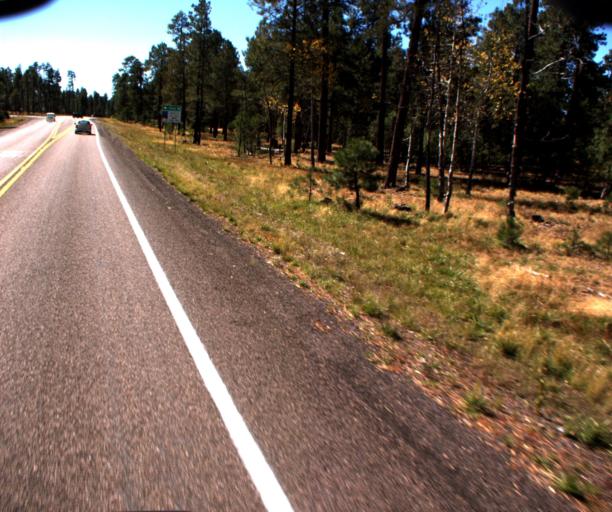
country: US
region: Arizona
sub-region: Navajo County
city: Heber-Overgaard
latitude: 34.3045
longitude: -110.8569
